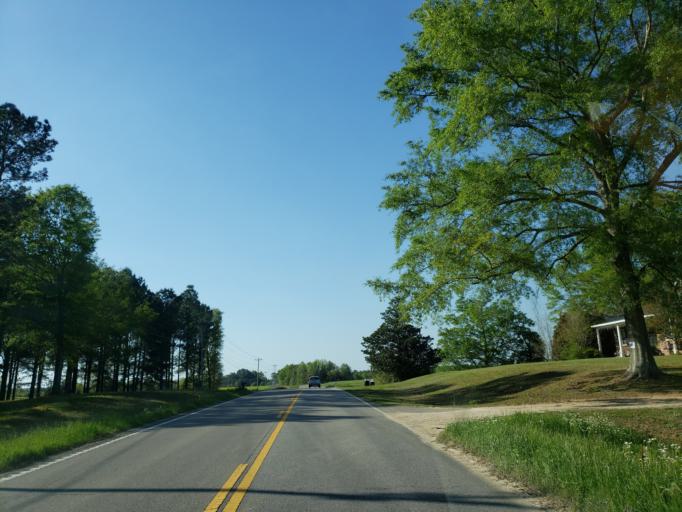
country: US
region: Mississippi
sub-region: Perry County
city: Richton
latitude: 31.4563
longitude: -88.9811
